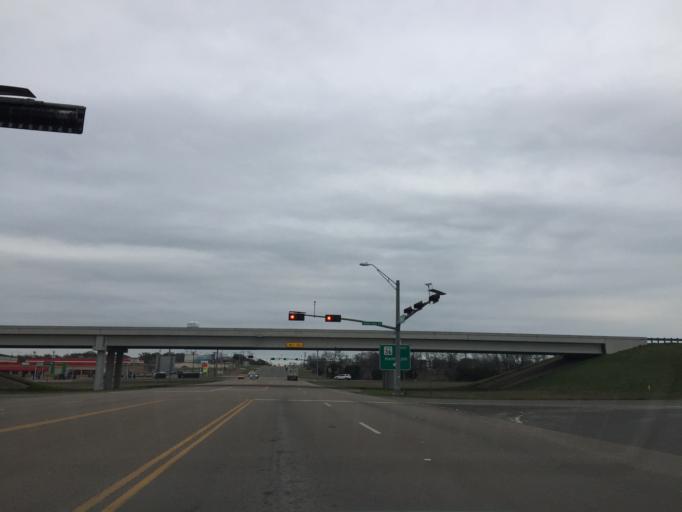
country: US
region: Texas
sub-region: Coryell County
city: Gatesville
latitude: 31.4346
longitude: -97.7160
